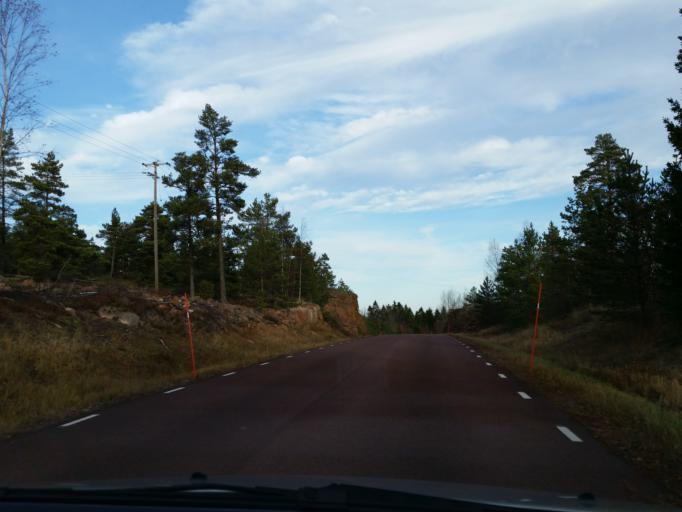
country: AX
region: Alands landsbygd
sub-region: Saltvik
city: Saltvik
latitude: 60.3393
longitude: 20.0971
